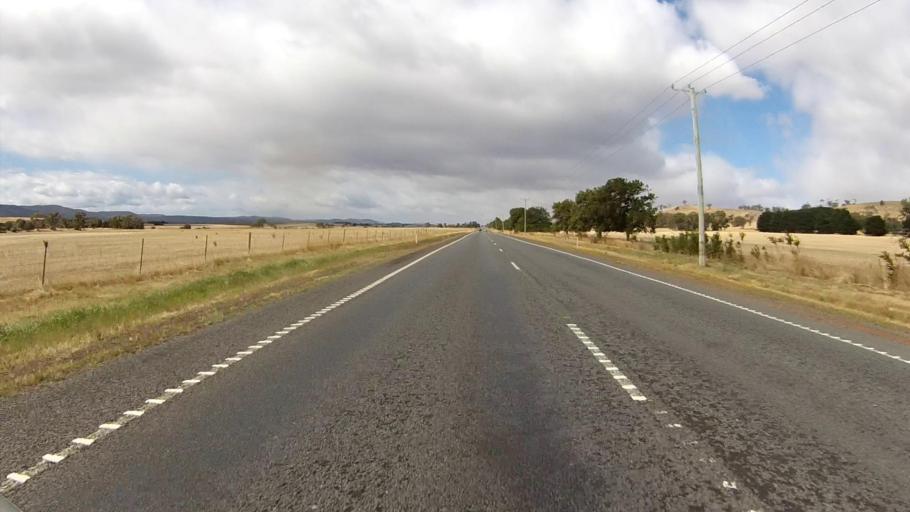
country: AU
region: Tasmania
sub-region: Northern Midlands
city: Evandale
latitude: -41.9648
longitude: 147.4997
